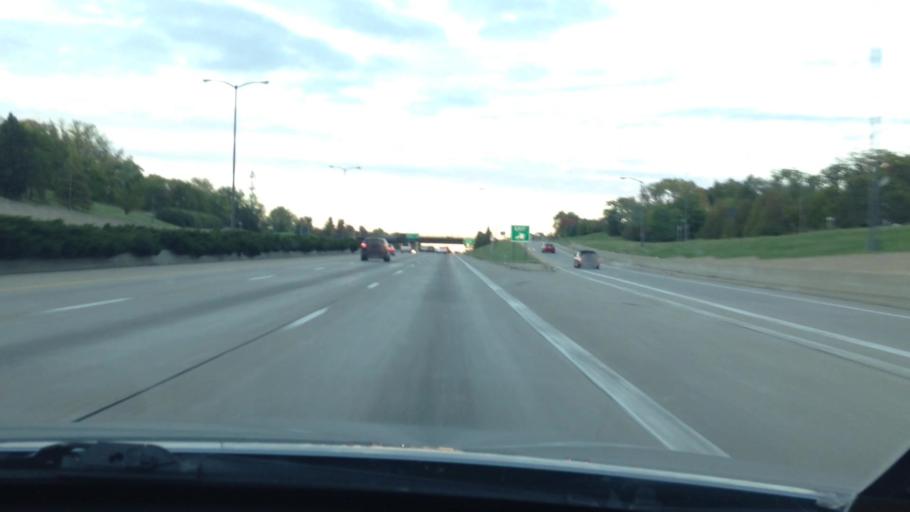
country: US
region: Missouri
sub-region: Jackson County
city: Kansas City
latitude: 39.0512
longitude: -94.5614
